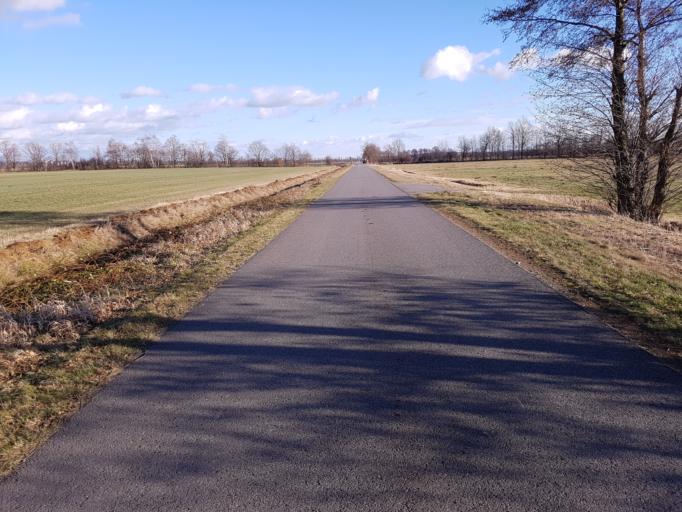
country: DE
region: Brandenburg
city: Groden
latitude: 51.4134
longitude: 13.5726
